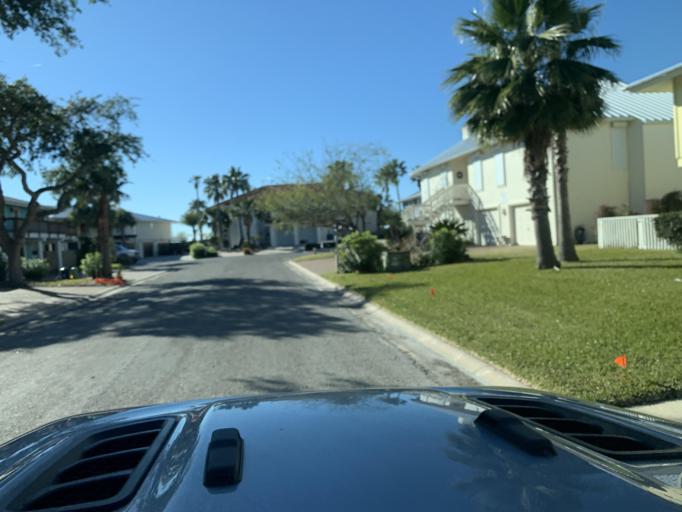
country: US
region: Texas
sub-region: Aransas County
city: Fulton
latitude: 28.0369
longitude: -97.0315
